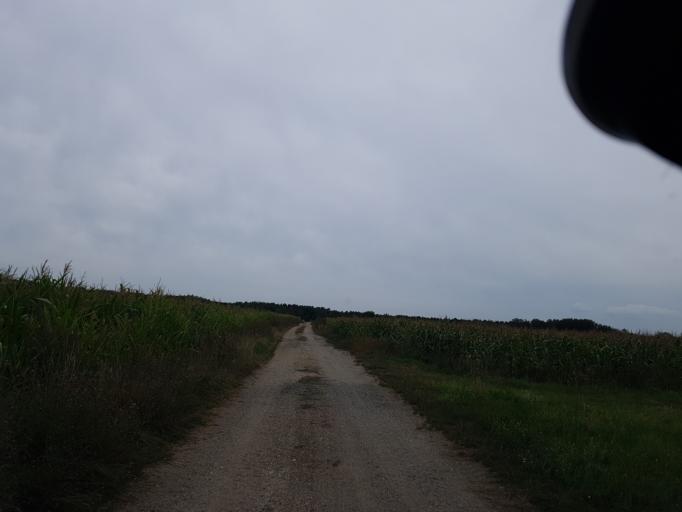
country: DE
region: Brandenburg
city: Finsterwalde
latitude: 51.6117
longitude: 13.6616
